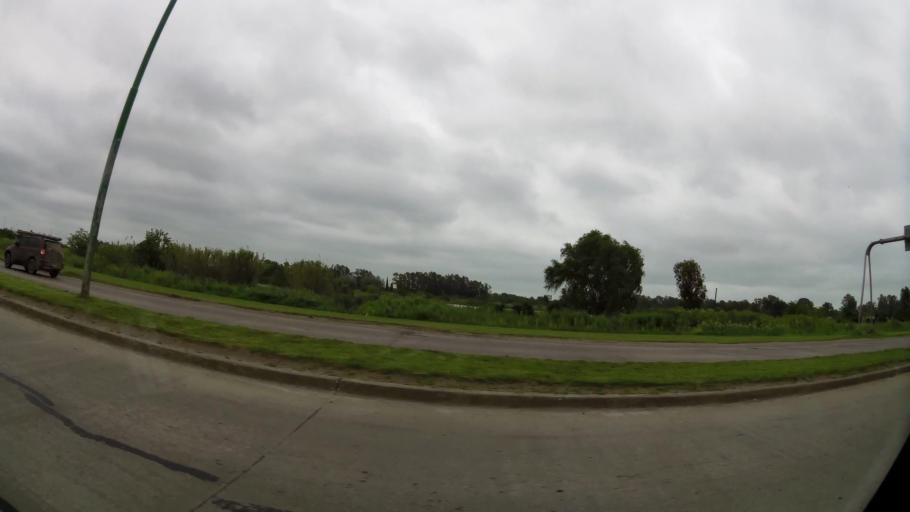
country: AR
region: Buenos Aires
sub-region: Partido de La Plata
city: La Plata
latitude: -35.0323
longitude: -58.0889
